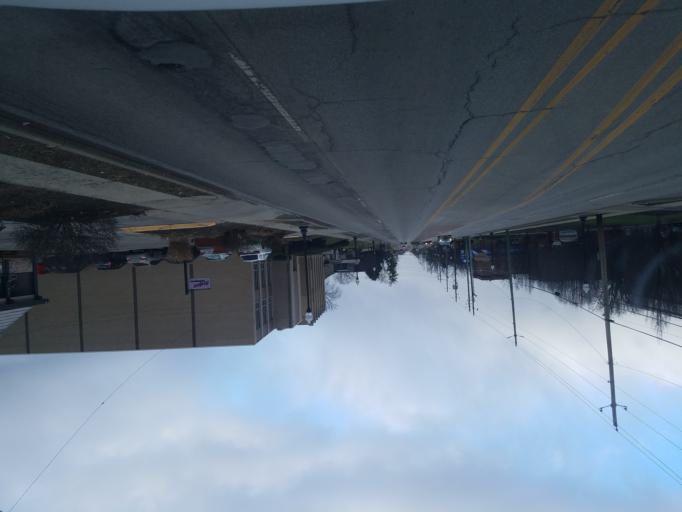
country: US
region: Indiana
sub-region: Marion County
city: Warren Park
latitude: 39.7708
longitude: -86.0696
